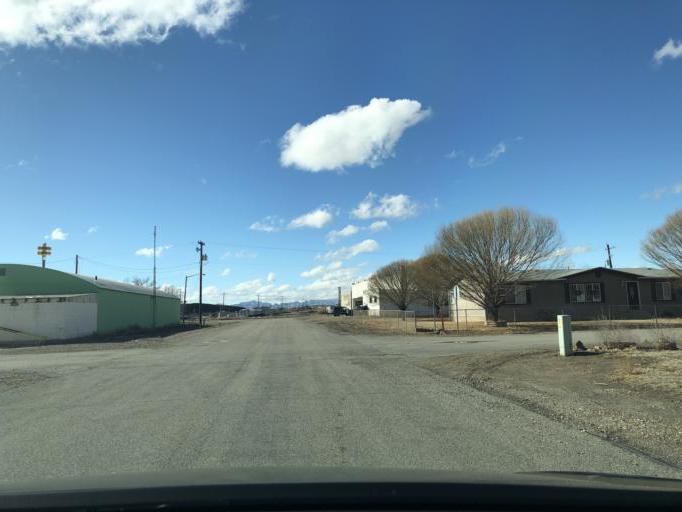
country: US
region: Utah
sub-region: Carbon County
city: East Carbon City
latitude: 38.9930
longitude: -110.1636
